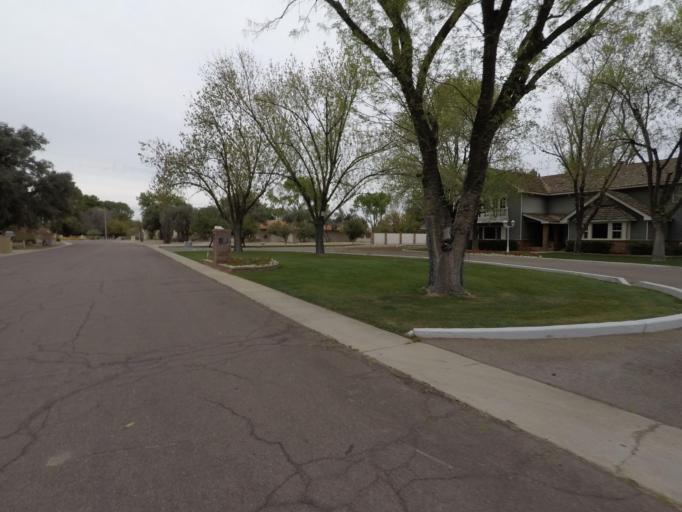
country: US
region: Arizona
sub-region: Maricopa County
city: Guadalupe
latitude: 33.3366
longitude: -111.9209
